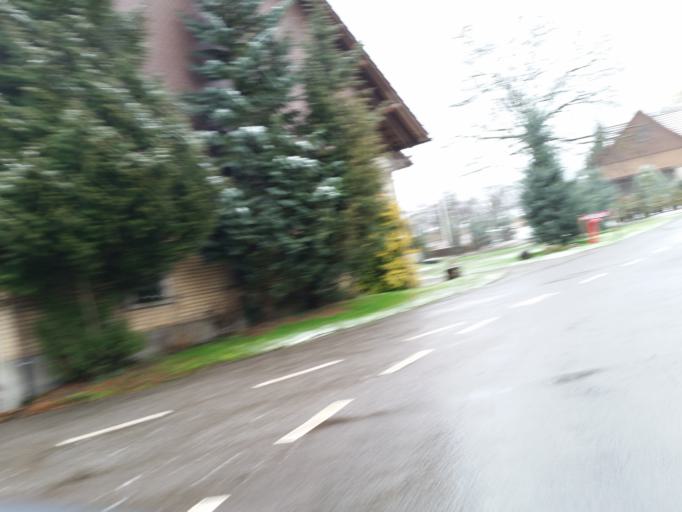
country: CH
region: Thurgau
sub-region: Arbon District
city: Egnach
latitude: 47.5269
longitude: 9.3873
